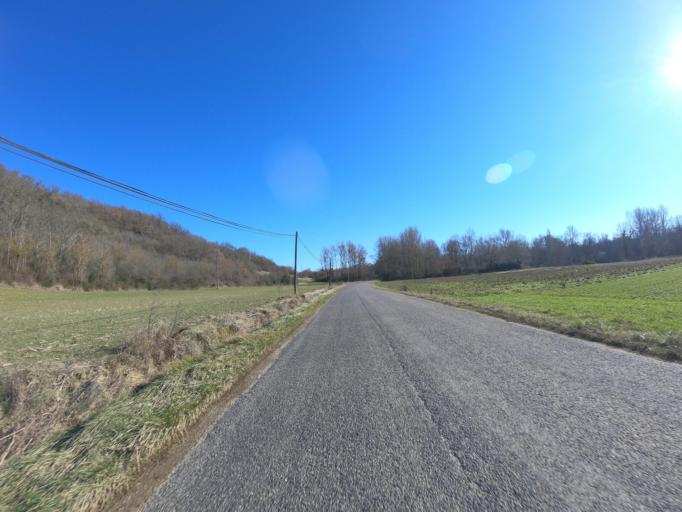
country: FR
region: Languedoc-Roussillon
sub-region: Departement de l'Aude
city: Belpech
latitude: 43.0929
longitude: 1.7637
